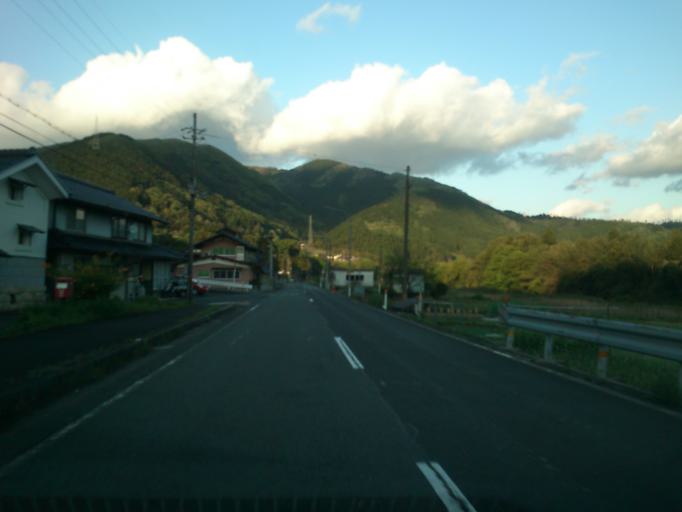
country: JP
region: Kyoto
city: Ayabe
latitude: 35.2707
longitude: 135.3877
